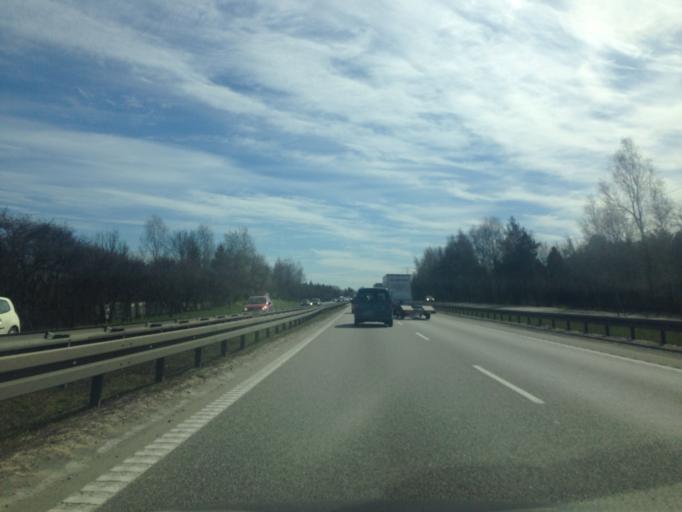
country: PL
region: Pomeranian Voivodeship
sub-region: Gdynia
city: Wielki Kack
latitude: 54.4089
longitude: 18.4860
